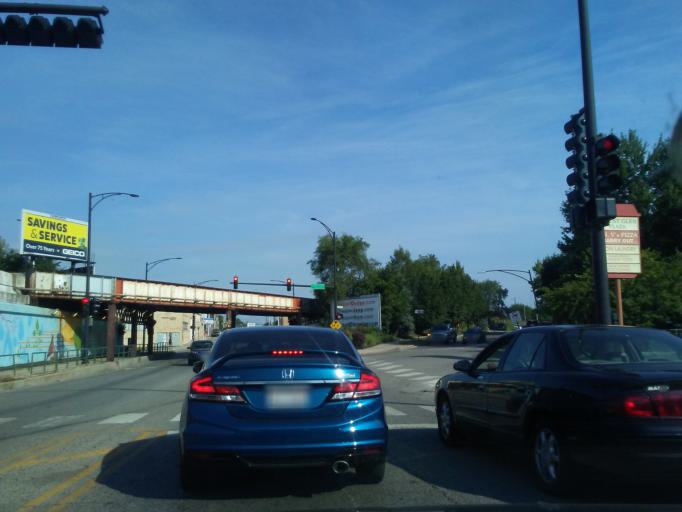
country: US
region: Illinois
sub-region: Cook County
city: Lincolnwood
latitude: 41.9769
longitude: -87.7544
